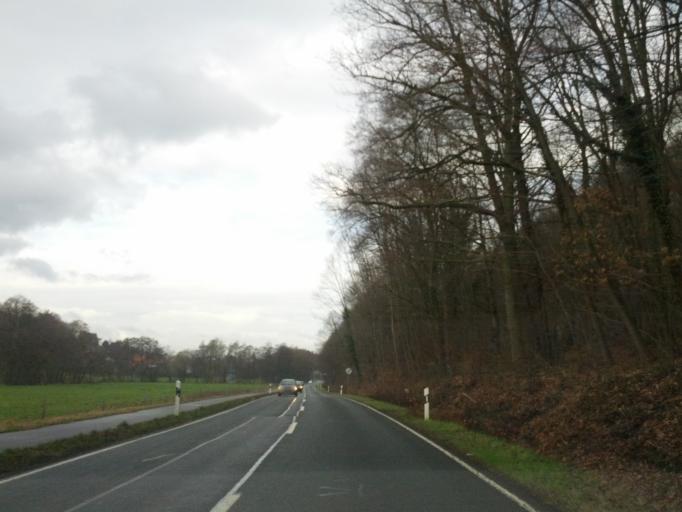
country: DE
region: Hesse
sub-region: Regierungsbezirk Kassel
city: Helsa
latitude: 51.2767
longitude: 9.6540
